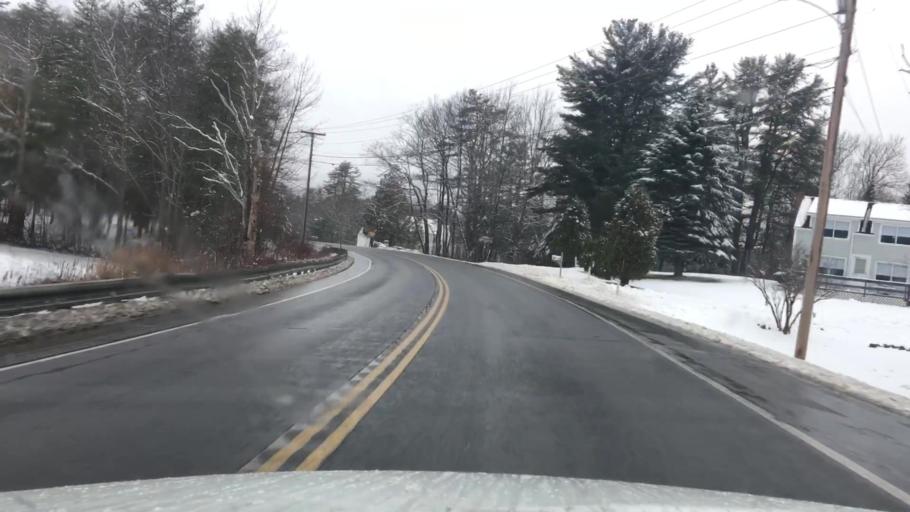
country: US
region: Maine
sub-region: Knox County
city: Rockport
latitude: 44.1777
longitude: -69.1280
